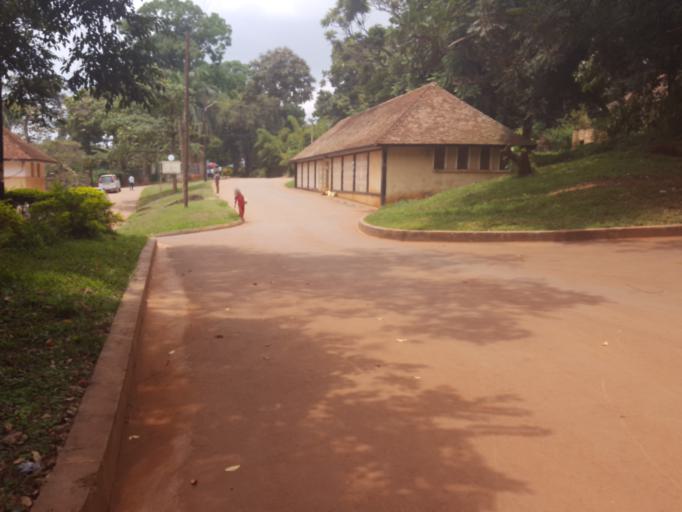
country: UG
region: Central Region
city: Kampala Central Division
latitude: 0.3389
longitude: 32.5674
